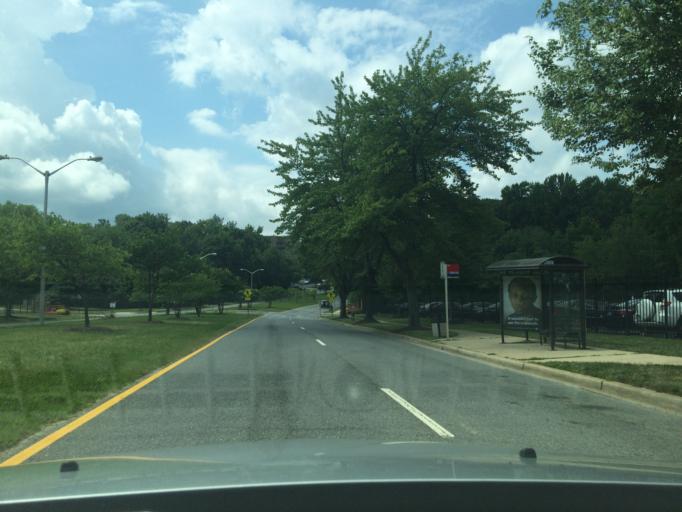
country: US
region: Maryland
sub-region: Prince George's County
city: Coral Hills
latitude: 38.8636
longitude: -76.9167
